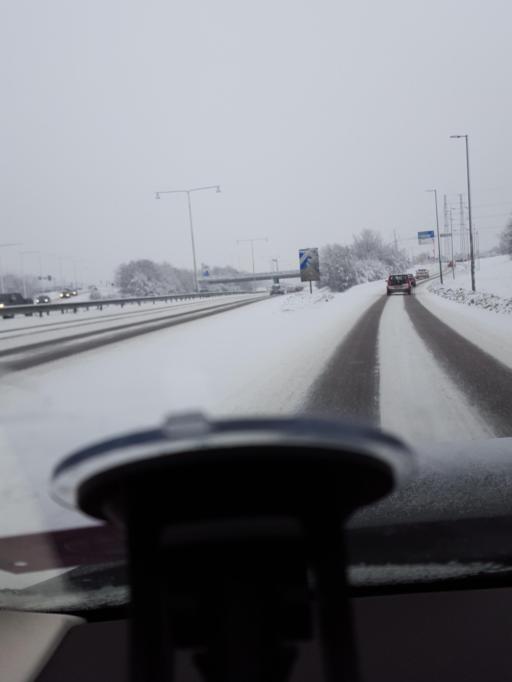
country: SE
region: Vaestra Goetaland
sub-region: Goteborg
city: Majorna
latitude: 57.6432
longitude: 11.9463
